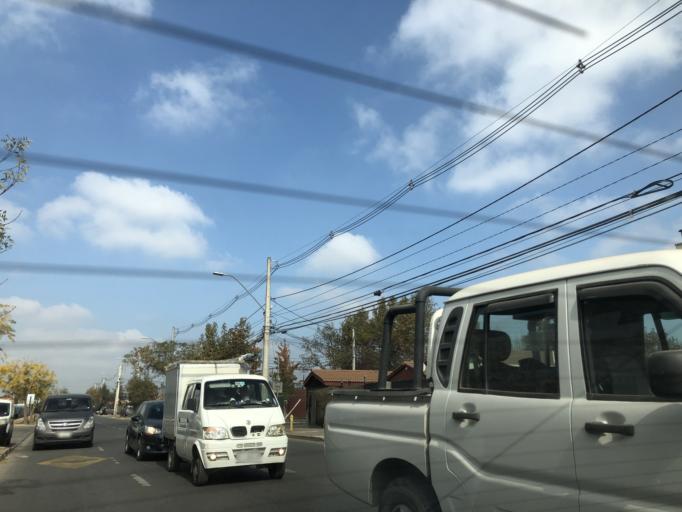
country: CL
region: Santiago Metropolitan
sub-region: Provincia de Cordillera
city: Puente Alto
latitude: -33.6021
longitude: -70.5880
